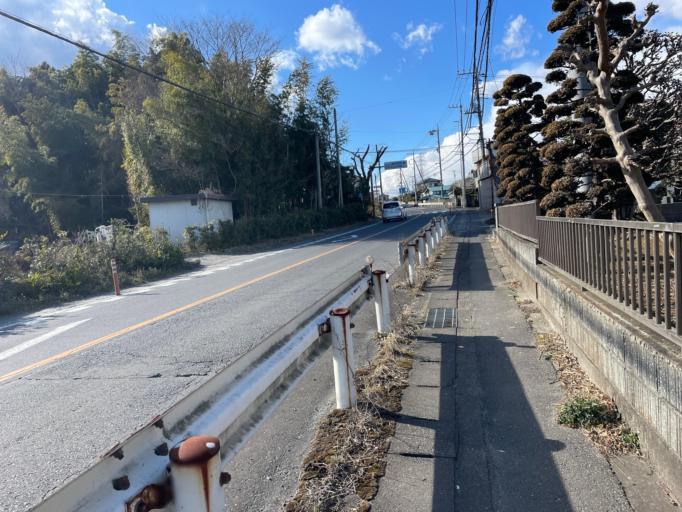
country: JP
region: Saitama
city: Ogawa
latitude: 36.0364
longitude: 139.3388
